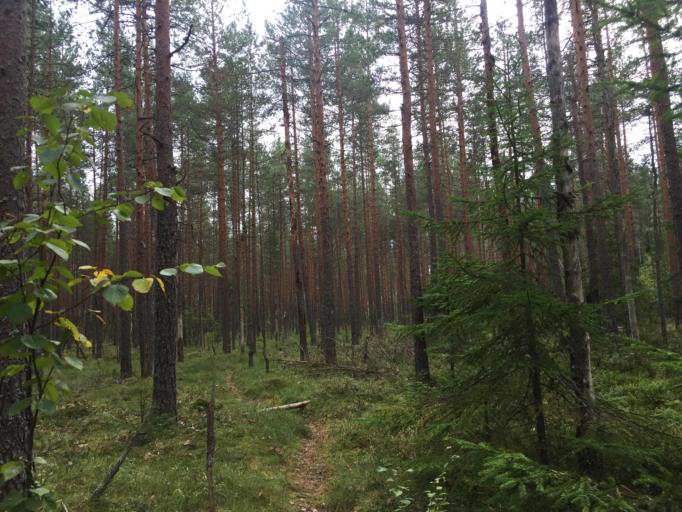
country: RU
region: Leningrad
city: Rozhdestveno
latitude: 59.2934
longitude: 30.0070
